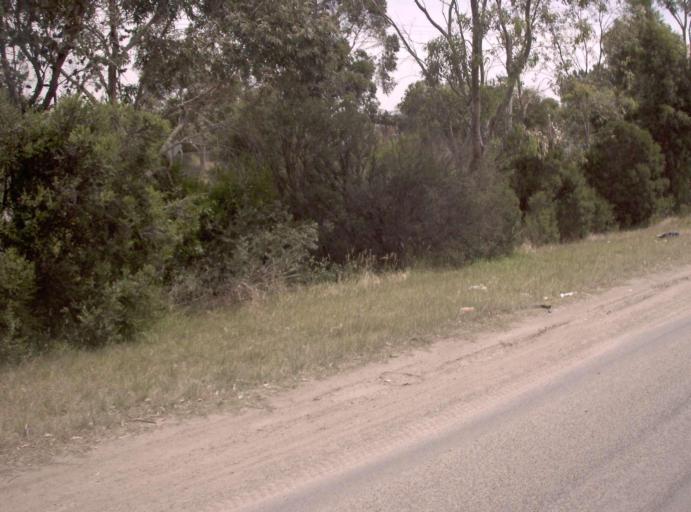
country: AU
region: Victoria
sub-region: Casey
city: Lynbrook
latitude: -38.0537
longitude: 145.2439
